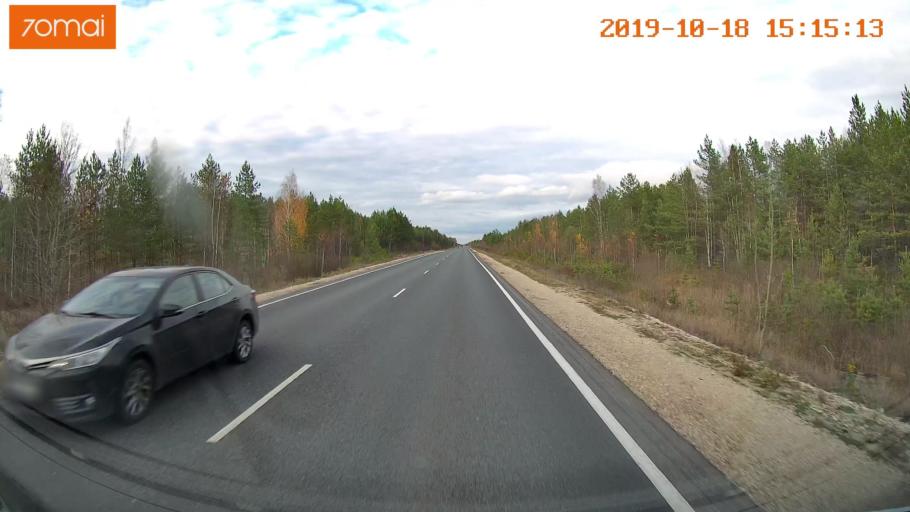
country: RU
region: Vladimir
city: Gus'-Khrustal'nyy
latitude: 55.6155
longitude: 40.7224
